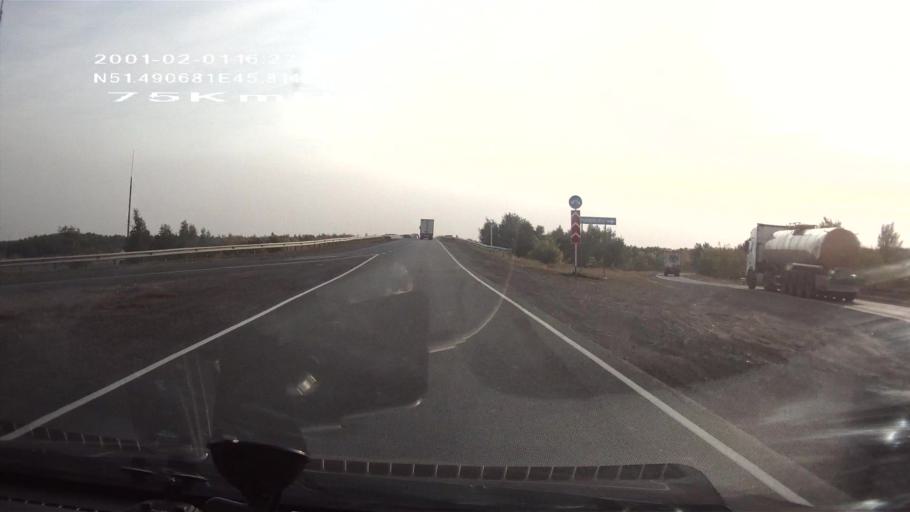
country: RU
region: Saratov
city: Sokolovyy
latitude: 51.4899
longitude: 45.8129
